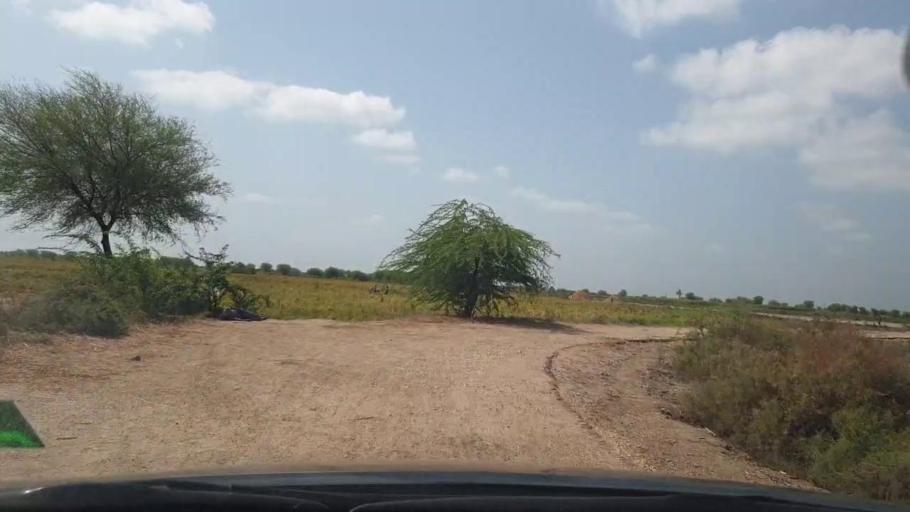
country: PK
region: Sindh
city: Tando Bago
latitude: 24.8356
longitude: 69.0452
